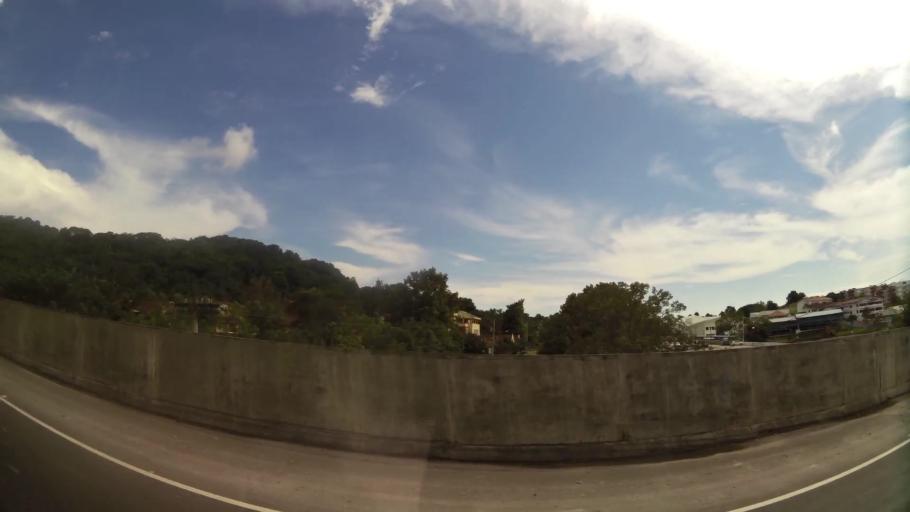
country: PA
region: Panama
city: San Miguelito
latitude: 9.0807
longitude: -79.4706
